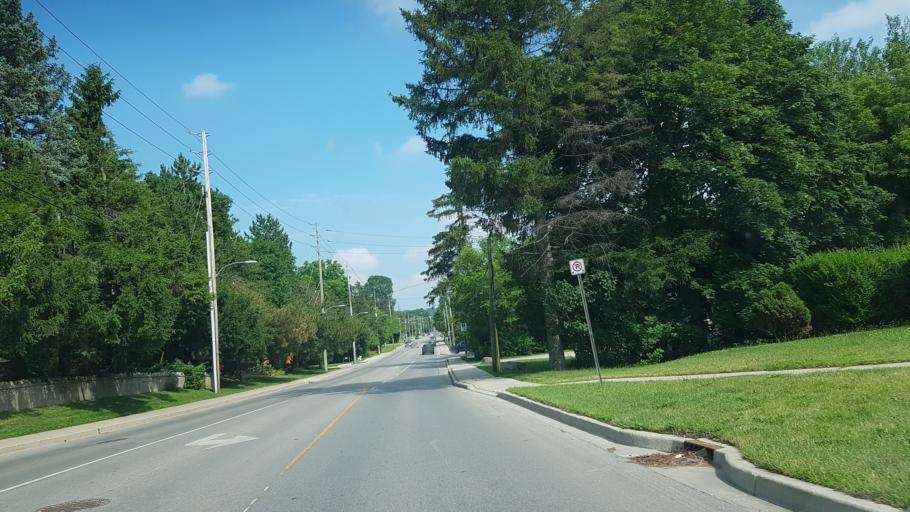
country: CA
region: Ontario
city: Delaware
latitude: 42.9632
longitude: -81.3439
